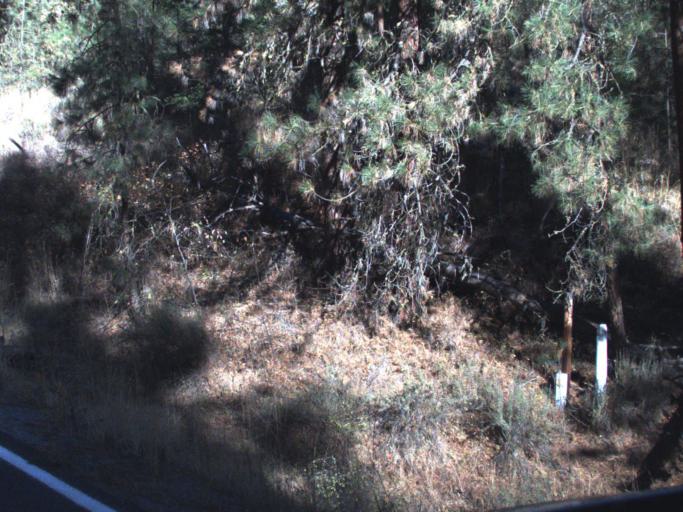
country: US
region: Washington
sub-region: Stevens County
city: Kettle Falls
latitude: 48.1935
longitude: -118.1713
